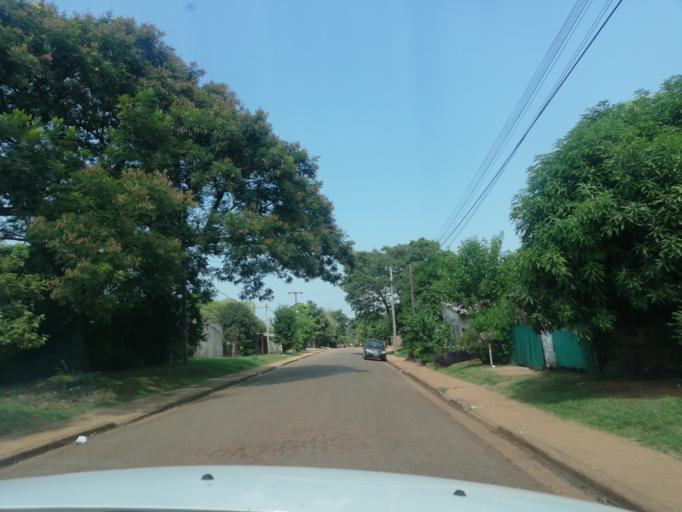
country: AR
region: Misiones
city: Garupa
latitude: -27.4432
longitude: -55.8874
